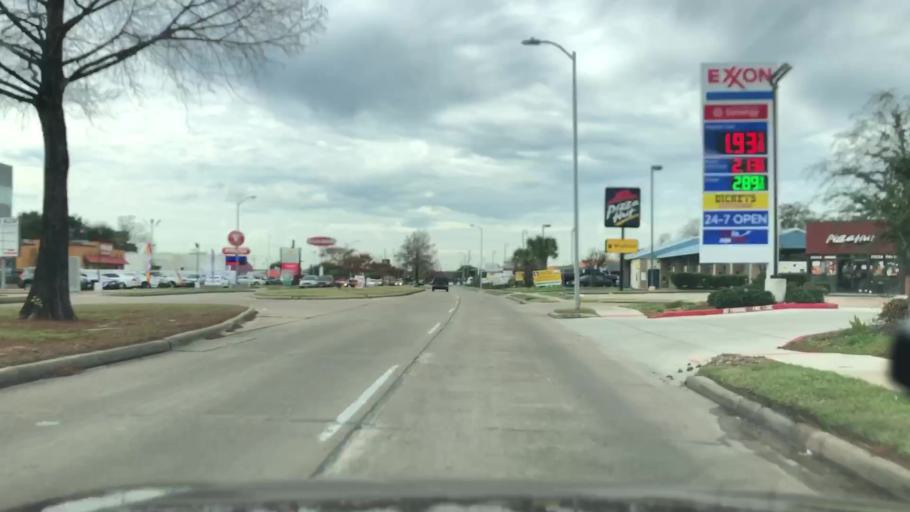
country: US
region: Texas
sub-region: Fort Bend County
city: Missouri City
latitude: 29.6559
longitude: -95.5242
